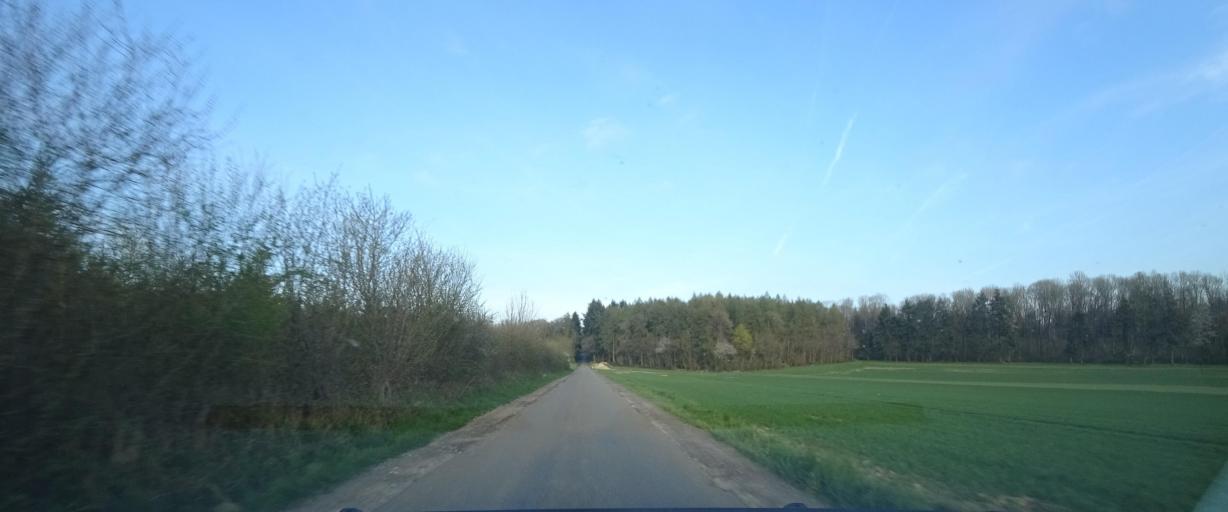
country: BE
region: Wallonia
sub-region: Province de Namur
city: Hamois
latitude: 50.3102
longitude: 5.1675
